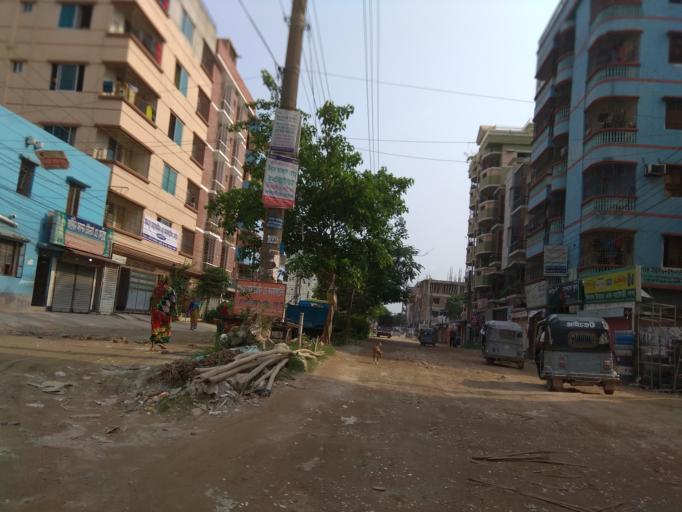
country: BD
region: Dhaka
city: Tungi
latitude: 23.8244
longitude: 90.3533
